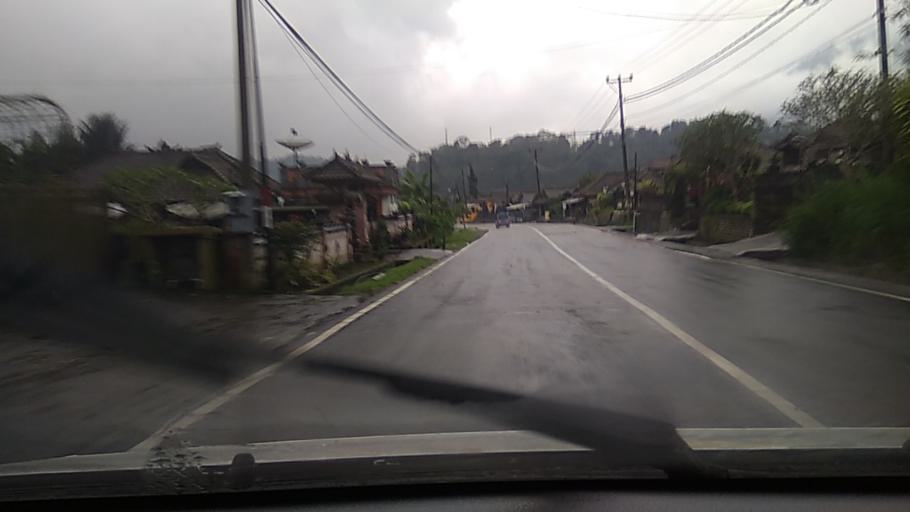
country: ID
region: Bali
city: Munduk
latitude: -8.2689
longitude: 115.1635
